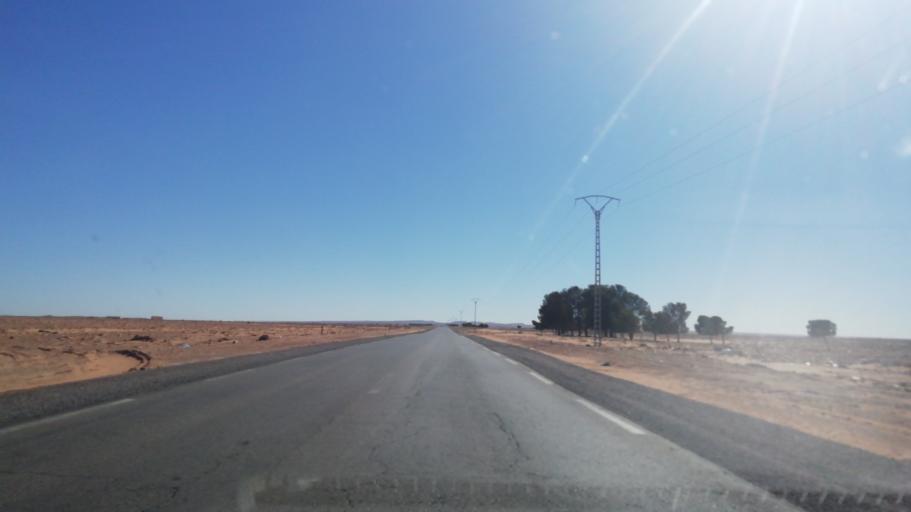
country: DZ
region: Saida
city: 'Ain el Hadjar
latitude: 34.0075
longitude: 0.1220
